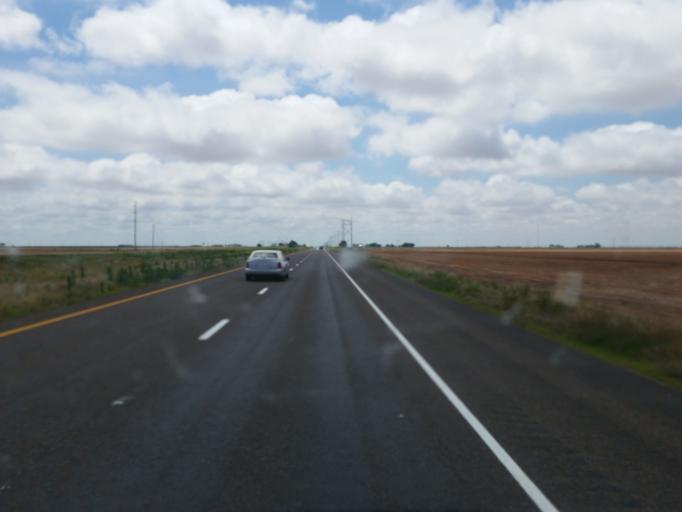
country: US
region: Texas
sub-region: Lubbock County
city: Slaton
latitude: 33.4106
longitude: -101.6276
